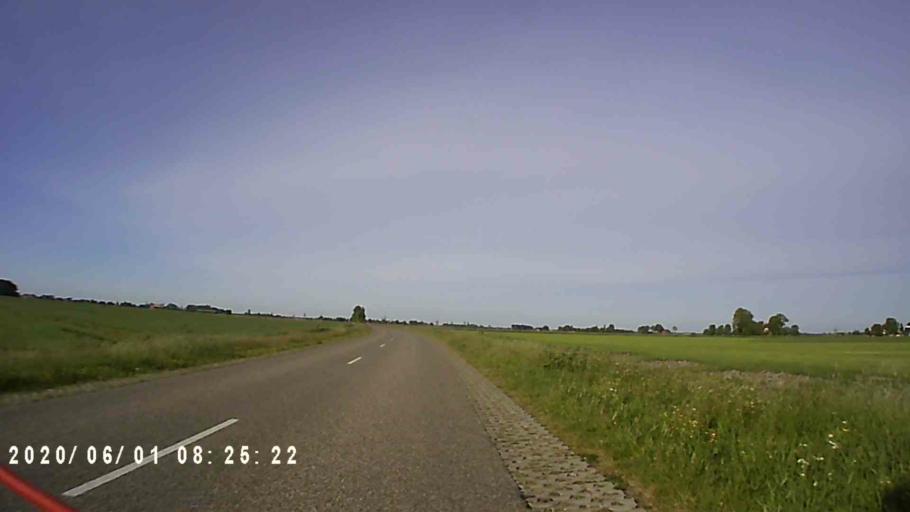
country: NL
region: Friesland
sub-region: Gemeente Ferwerderadiel
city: Burdaard
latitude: 53.3008
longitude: 5.8656
